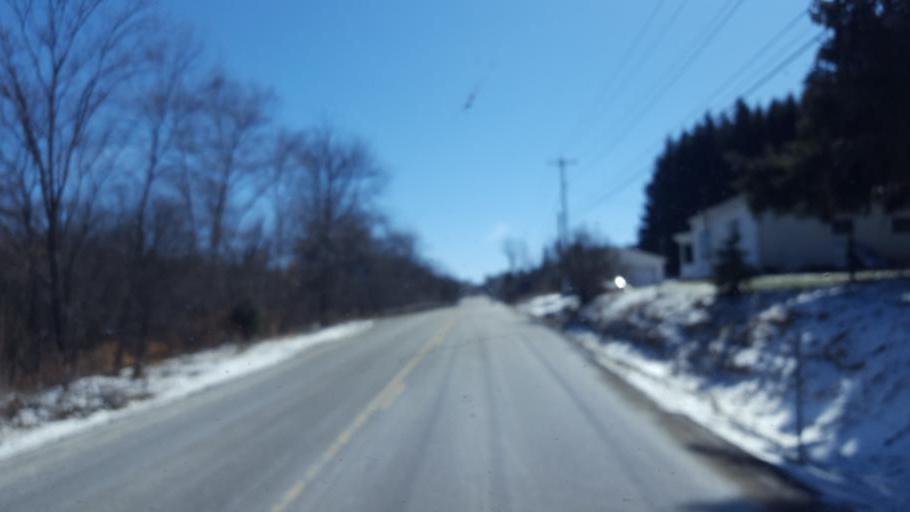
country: US
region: New York
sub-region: Allegany County
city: Andover
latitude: 42.0750
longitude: -77.8516
